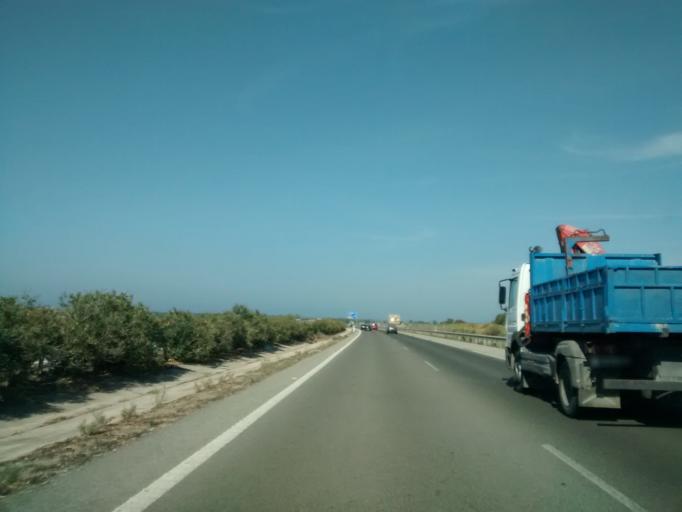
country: ES
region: Andalusia
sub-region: Provincia de Cadiz
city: Conil de la Frontera
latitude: 36.3551
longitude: -6.0824
